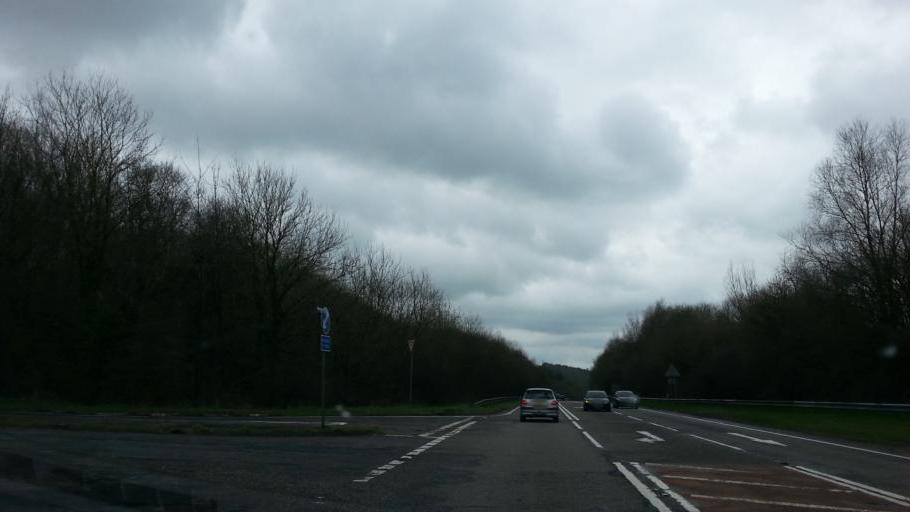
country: GB
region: England
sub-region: Devon
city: South Molton
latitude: 51.0488
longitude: -3.9178
